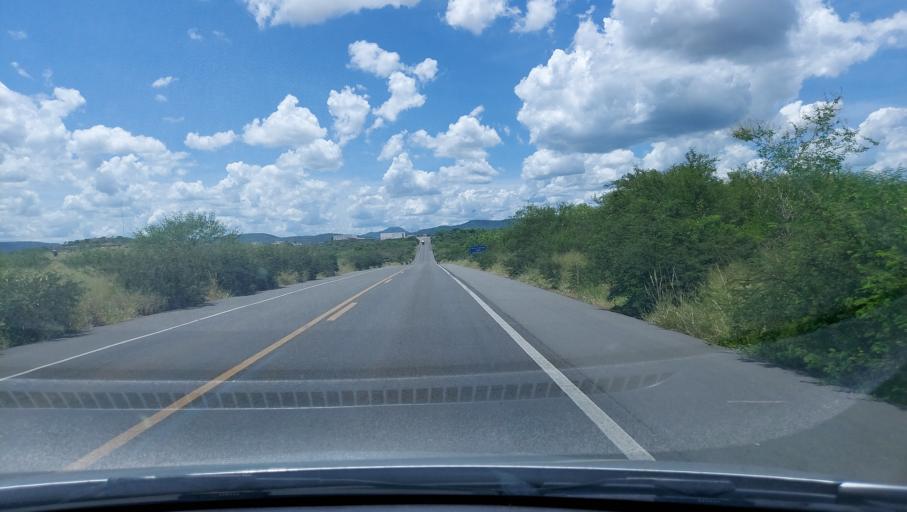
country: BR
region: Bahia
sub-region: Itaberaba
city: Itaberaba
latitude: -12.5211
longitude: -40.2686
